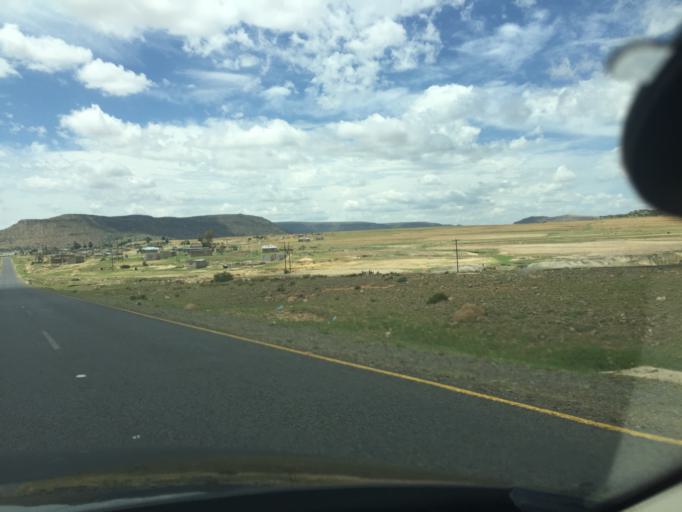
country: LS
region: Mafeteng
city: Mafeteng
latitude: -29.9341
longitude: 27.2616
